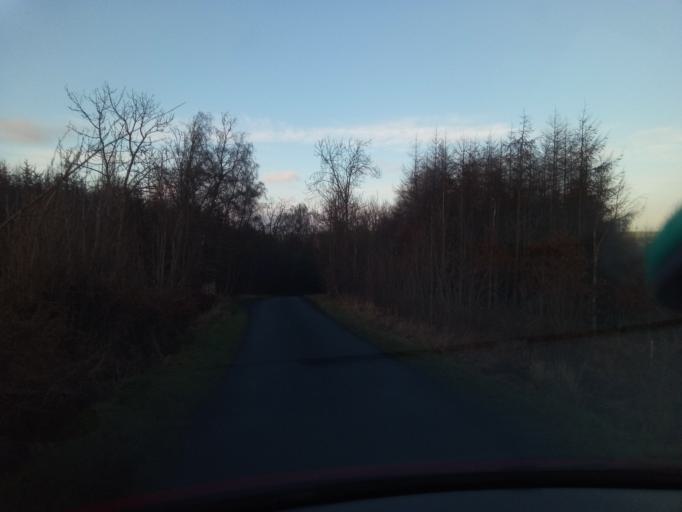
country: GB
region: Scotland
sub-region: The Scottish Borders
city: Melrose
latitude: 55.5849
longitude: -2.7399
